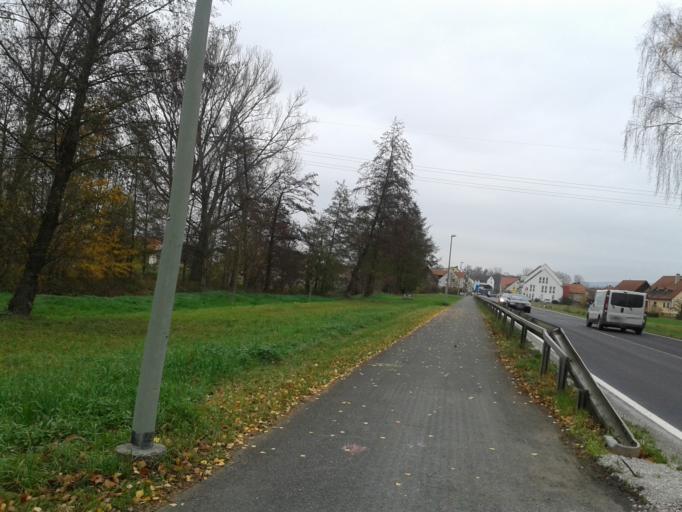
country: DE
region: Bavaria
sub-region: Upper Franconia
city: Memmelsdorf
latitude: 49.9392
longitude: 10.9666
